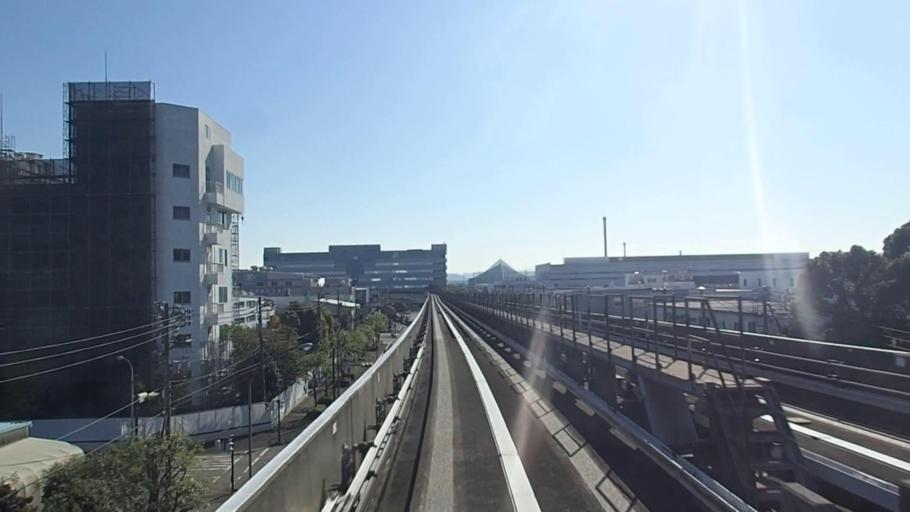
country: JP
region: Kanagawa
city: Yokosuka
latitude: 35.3490
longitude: 139.6486
